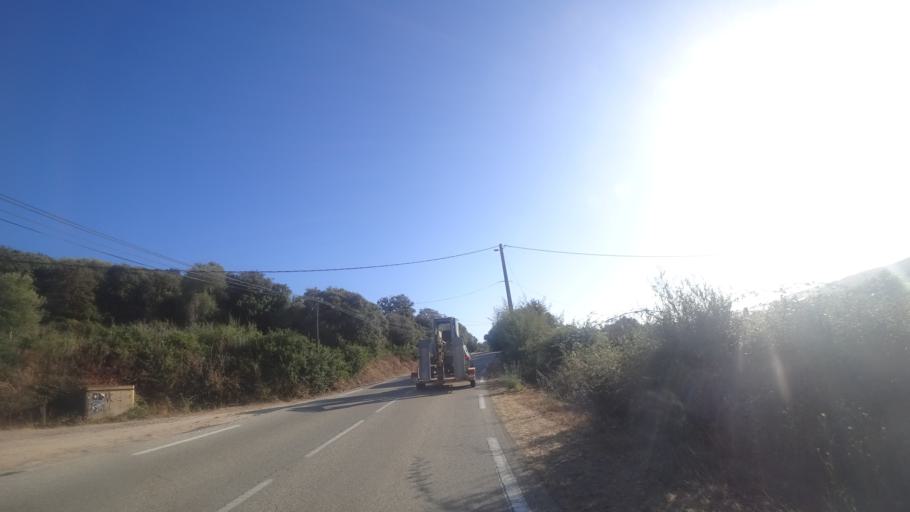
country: FR
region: Corsica
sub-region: Departement de la Corse-du-Sud
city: Cargese
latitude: 42.1497
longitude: 8.6054
